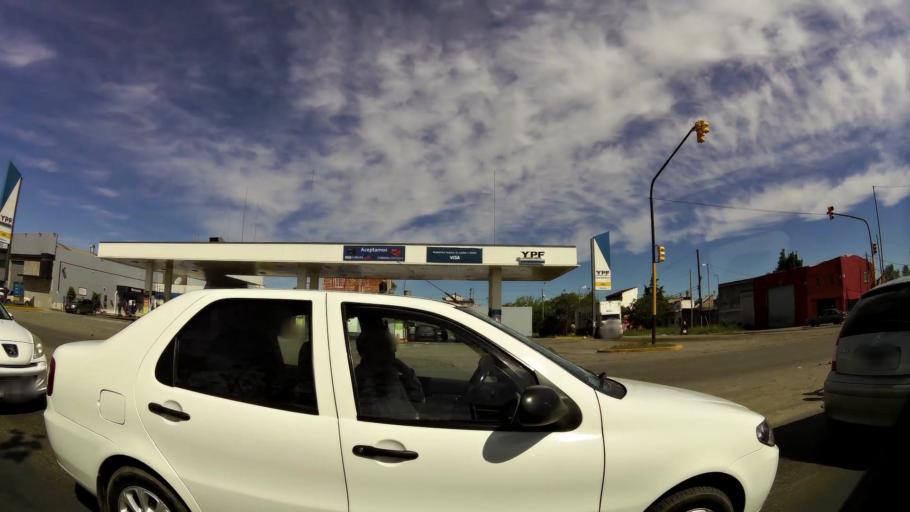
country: AR
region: Buenos Aires
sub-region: Partido de Quilmes
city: Quilmes
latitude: -34.7851
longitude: -58.3015
